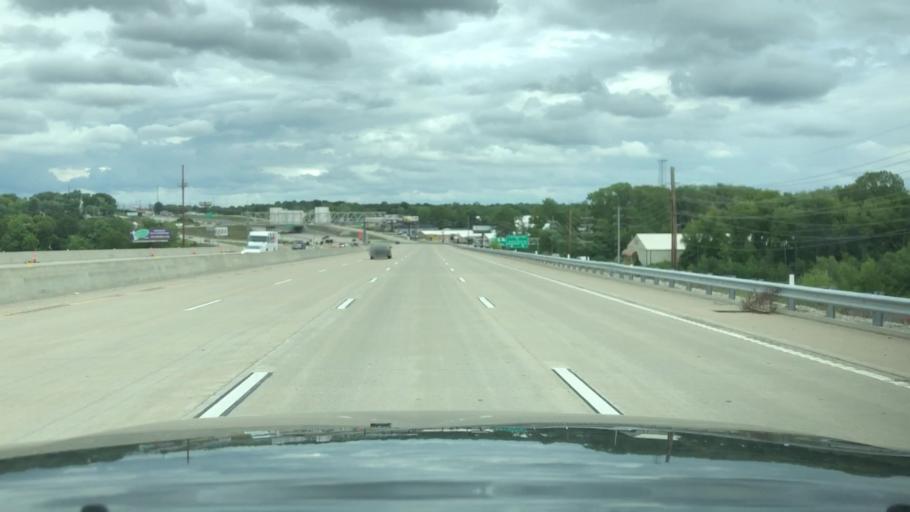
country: US
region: Missouri
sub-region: Saint Charles County
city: Cottleville
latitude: 38.7403
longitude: -90.6168
